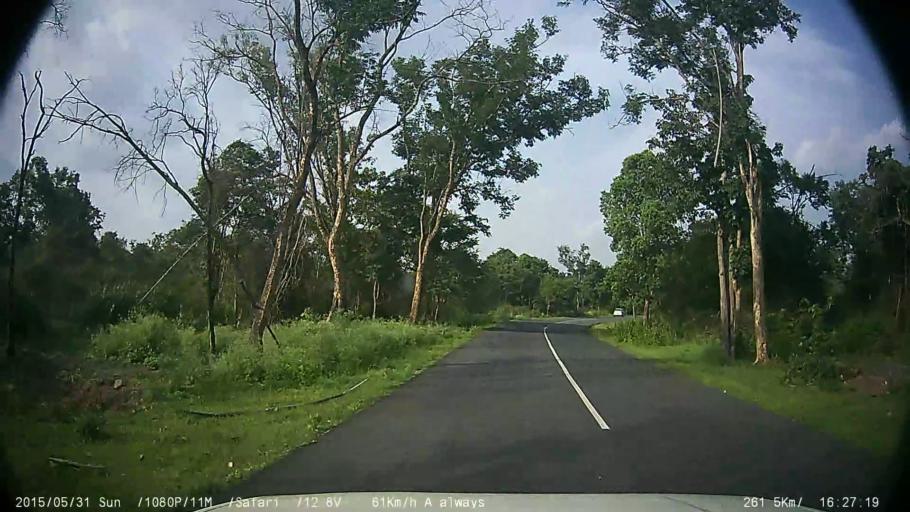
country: IN
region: Karnataka
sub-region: Chamrajnagar
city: Gundlupet
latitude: 11.7667
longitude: 76.5342
